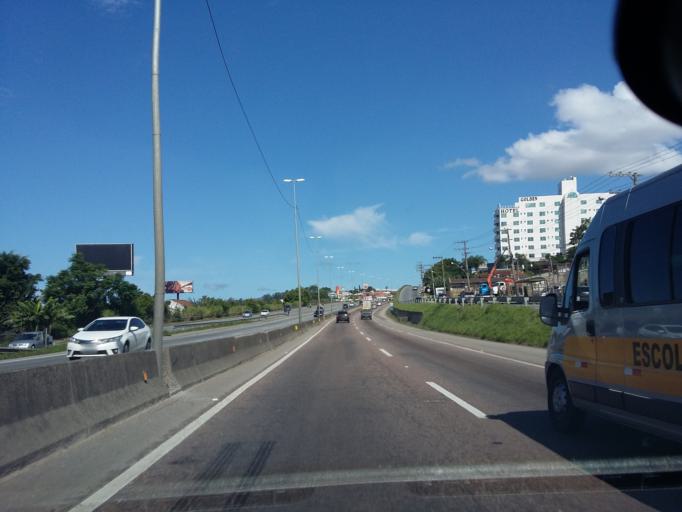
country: BR
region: Santa Catarina
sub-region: Biguacu
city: Biguacu
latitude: -27.5391
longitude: -48.6239
